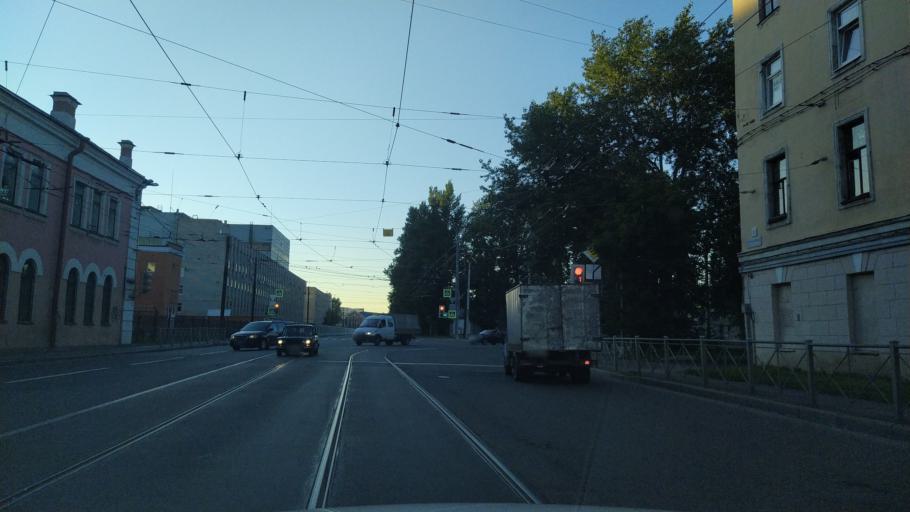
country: RU
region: Leningrad
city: Finlyandskiy
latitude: 59.9565
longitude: 30.3730
